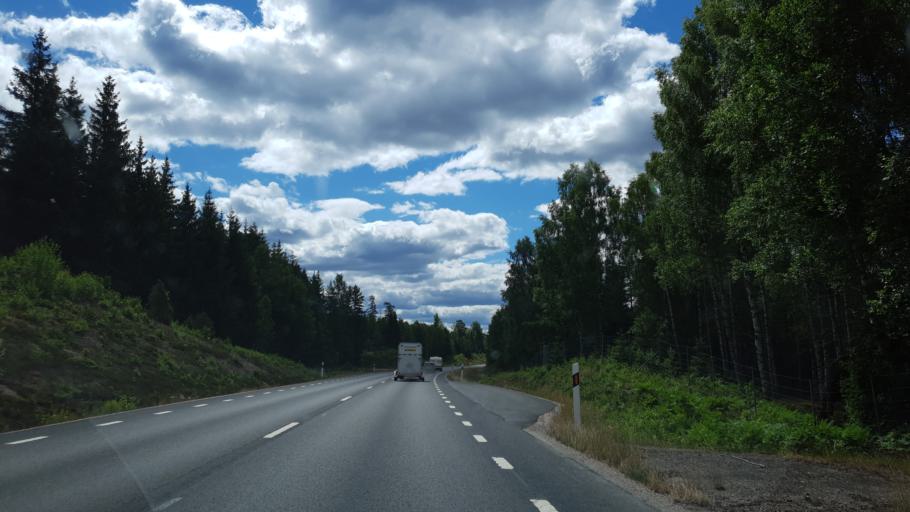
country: SE
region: Kronoberg
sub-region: Vaxjo Kommun
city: Braas
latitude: 57.2113
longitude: 15.1524
